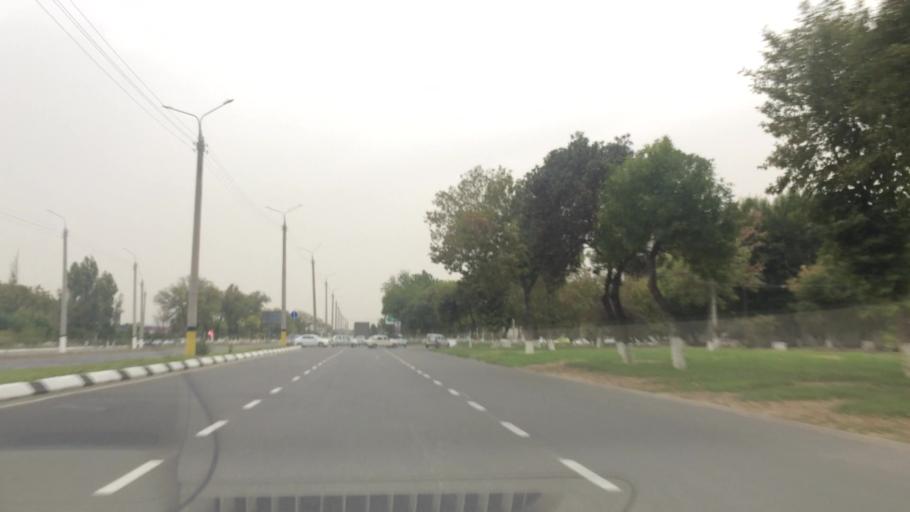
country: UZ
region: Toshkent
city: Salor
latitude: 41.3133
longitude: 69.3498
